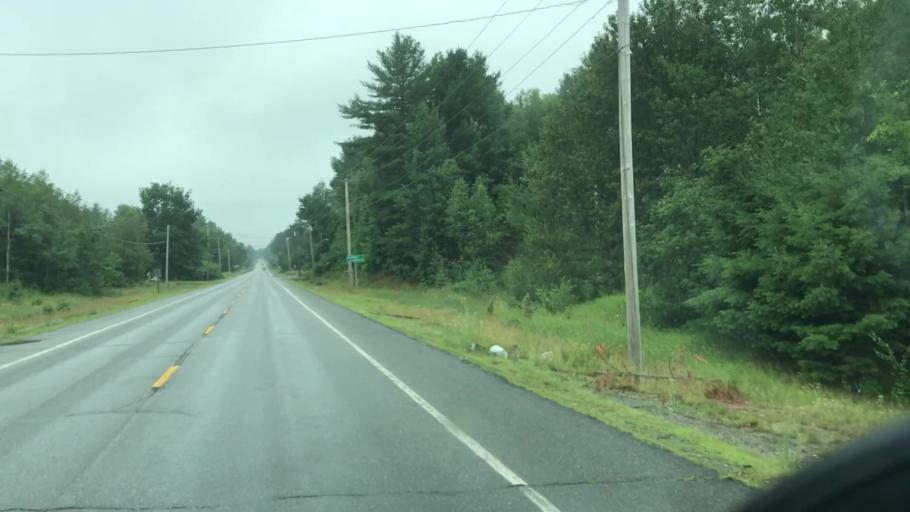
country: US
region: Maine
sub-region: Penobscot County
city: Lincoln
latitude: 45.3353
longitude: -68.5786
